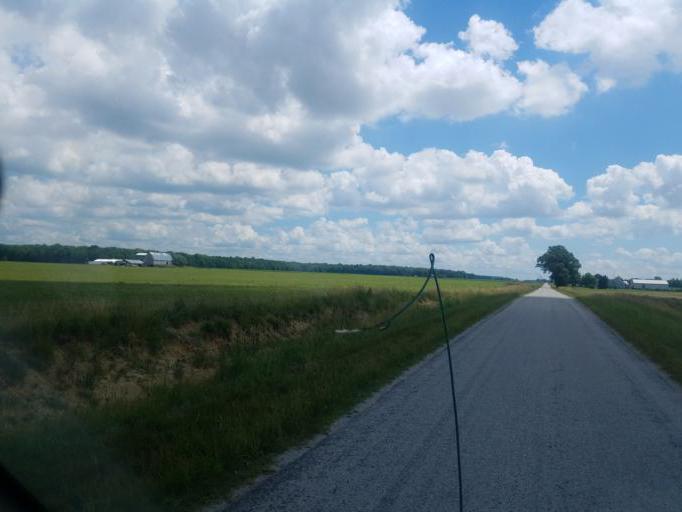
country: US
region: Ohio
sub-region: Huron County
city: Willard
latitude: 40.9946
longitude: -82.8351
